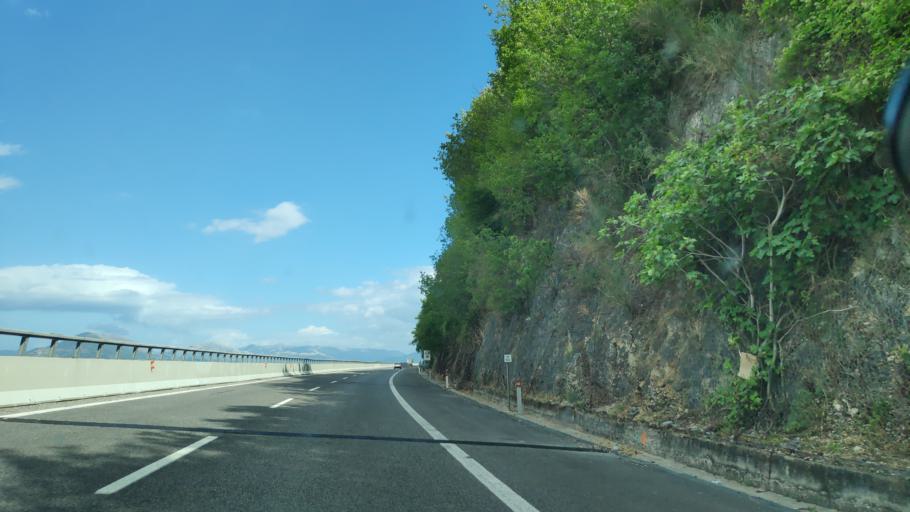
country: IT
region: Campania
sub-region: Provincia di Salerno
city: Sicignano degli Alburni
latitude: 40.5980
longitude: 15.3165
